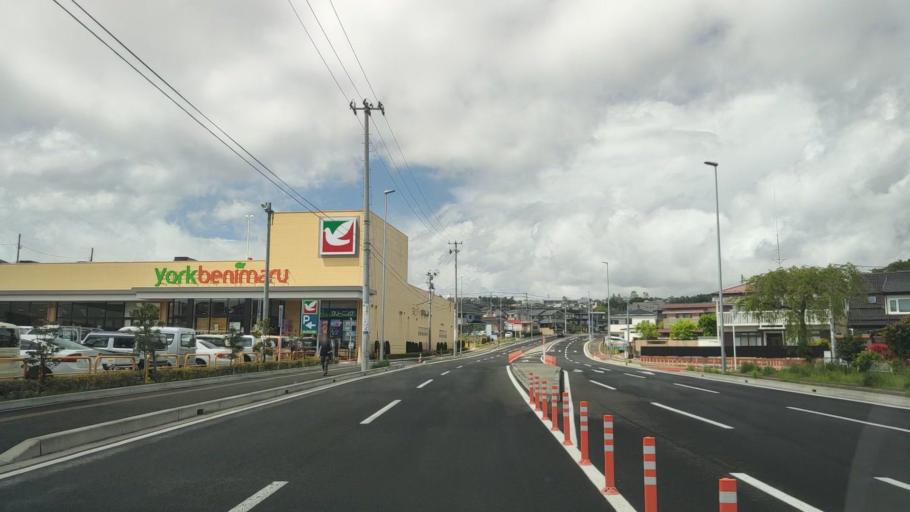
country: JP
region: Miyagi
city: Sendai
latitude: 38.2311
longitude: 140.8550
